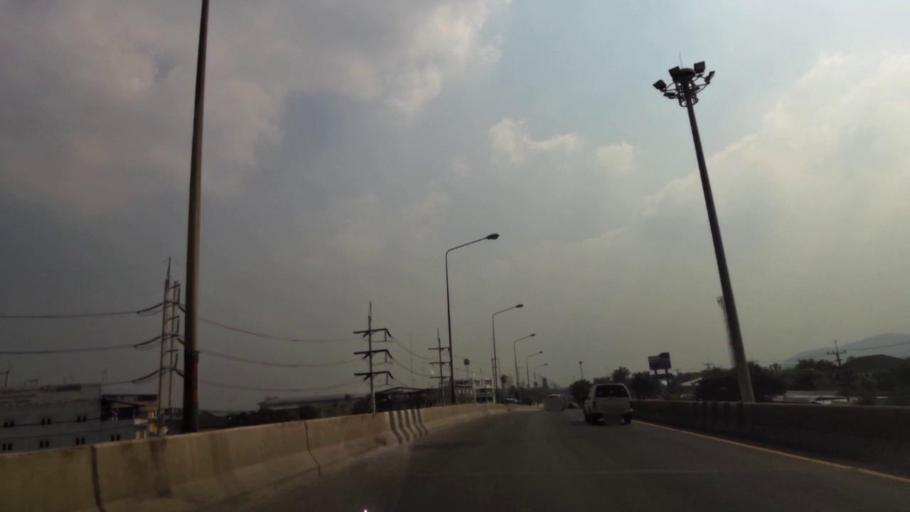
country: TH
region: Chon Buri
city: Ban Bueng
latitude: 13.3165
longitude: 101.1043
